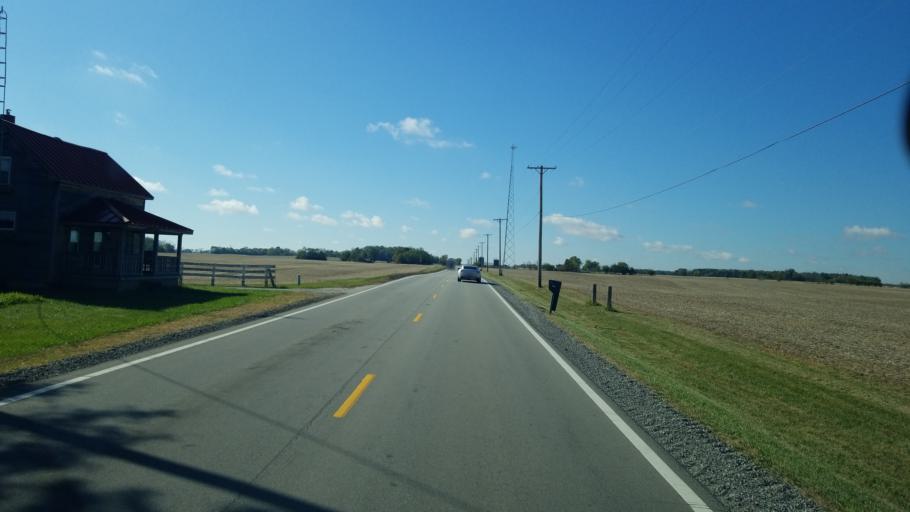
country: US
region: Ohio
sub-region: Highland County
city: Leesburg
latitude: 39.4379
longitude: -83.5096
